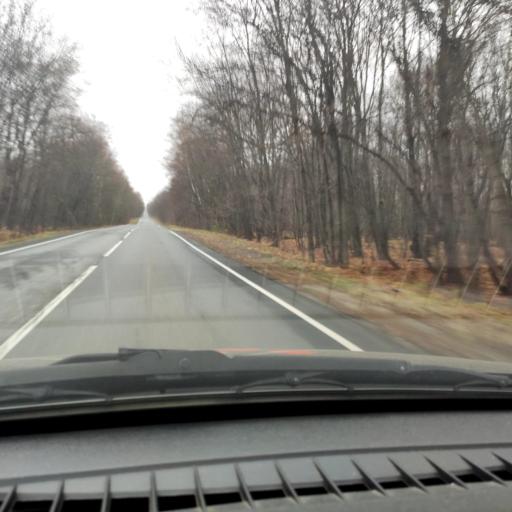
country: RU
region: Samara
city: Zhigulevsk
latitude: 53.3485
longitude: 49.5796
